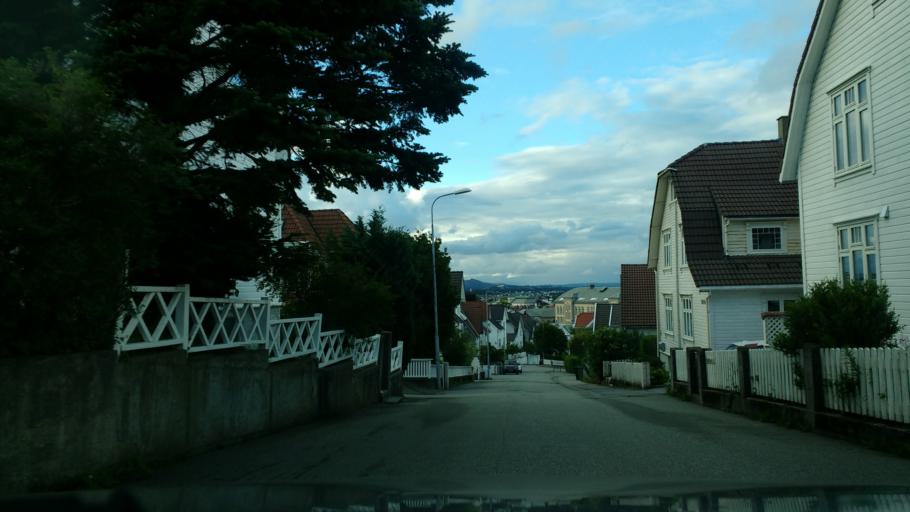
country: NO
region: Rogaland
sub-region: Stavanger
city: Stavanger
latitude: 58.9594
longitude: 5.7315
